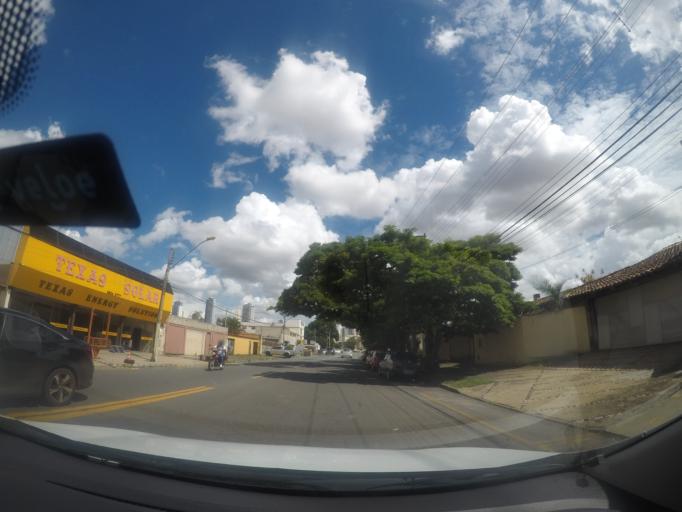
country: BR
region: Goias
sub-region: Goiania
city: Goiania
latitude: -16.6800
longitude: -49.2779
